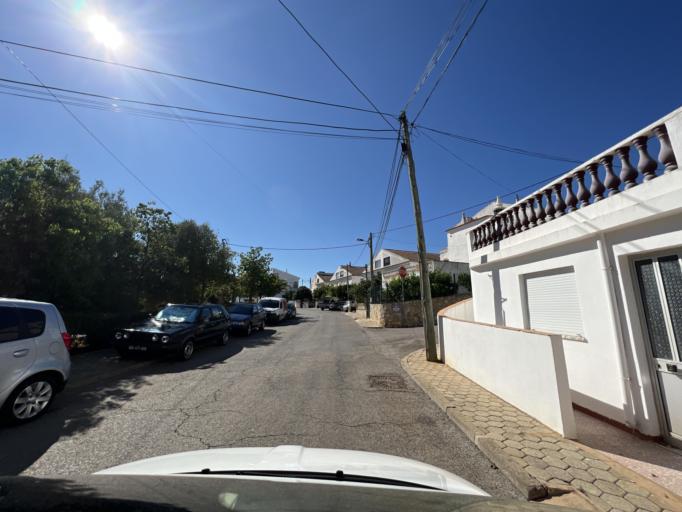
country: PT
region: Faro
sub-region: Lagoa
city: Estombar
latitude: 37.1432
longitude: -8.5100
